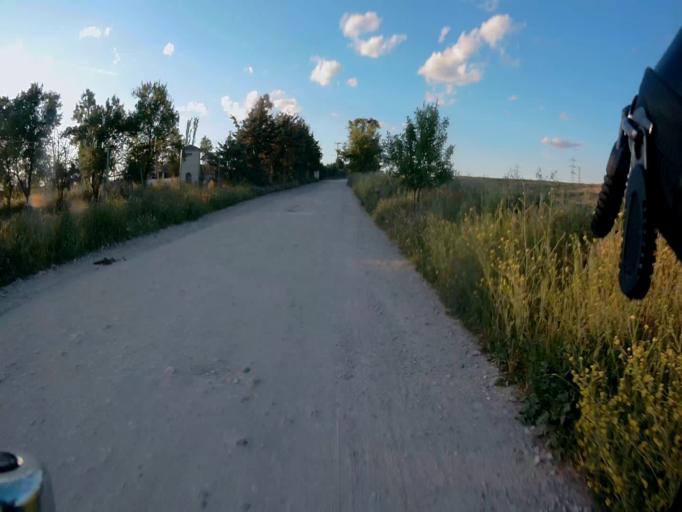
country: ES
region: Madrid
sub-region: Provincia de Madrid
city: Leganes
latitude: 40.3289
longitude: -3.7950
